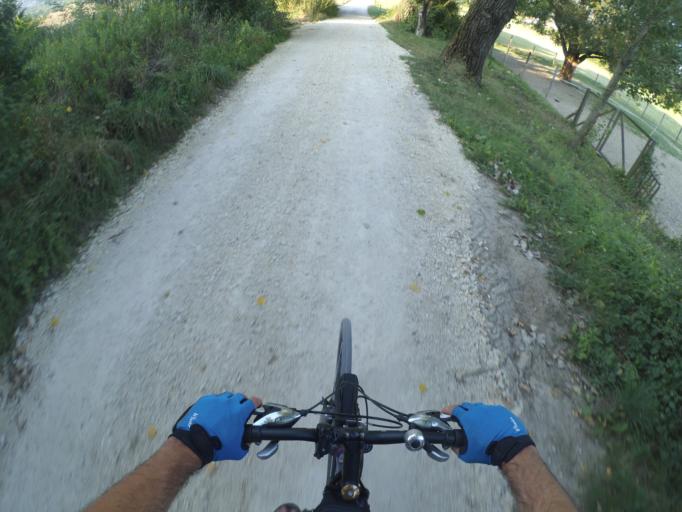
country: HU
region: Pest
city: Pilisszanto
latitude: 47.6632
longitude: 18.8814
